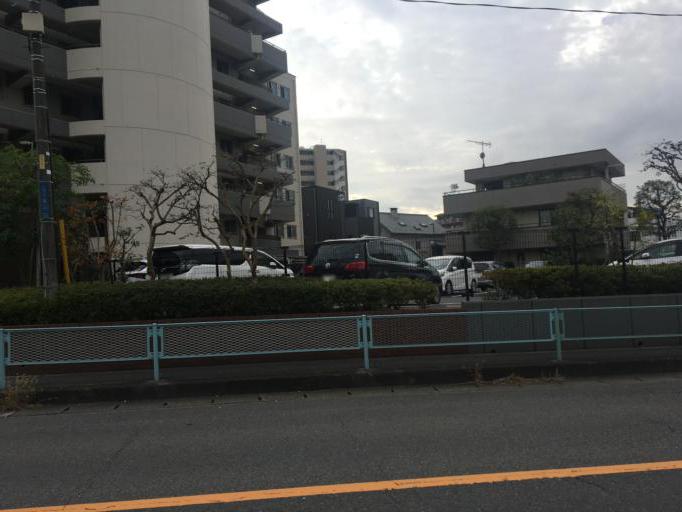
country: JP
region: Saitama
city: Shiki
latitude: 35.8182
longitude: 139.5777
